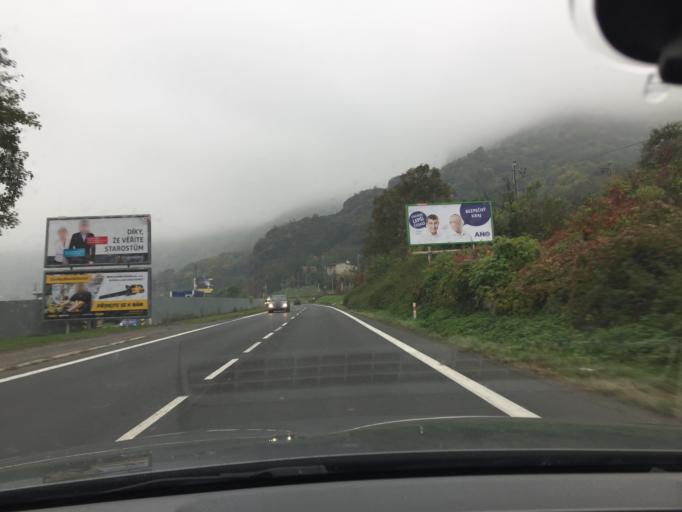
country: CZ
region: Ustecky
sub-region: Okres Usti nad Labem
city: Usti nad Labem
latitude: 50.6356
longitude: 14.0471
